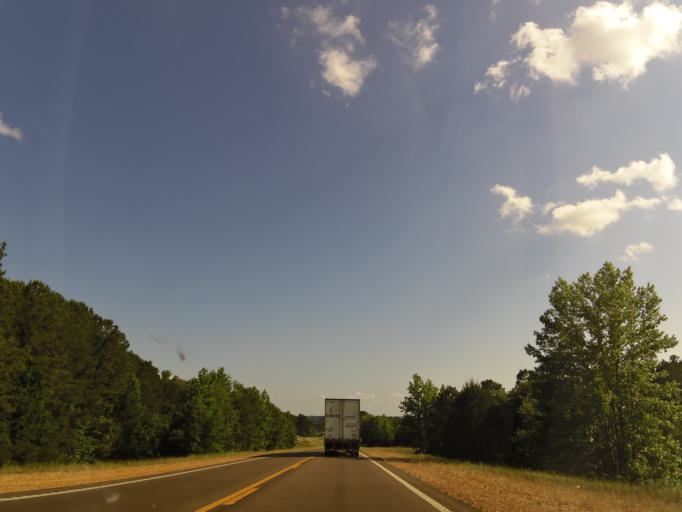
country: US
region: Mississippi
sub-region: Lafayette County
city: University
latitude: 34.2889
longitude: -89.5203
